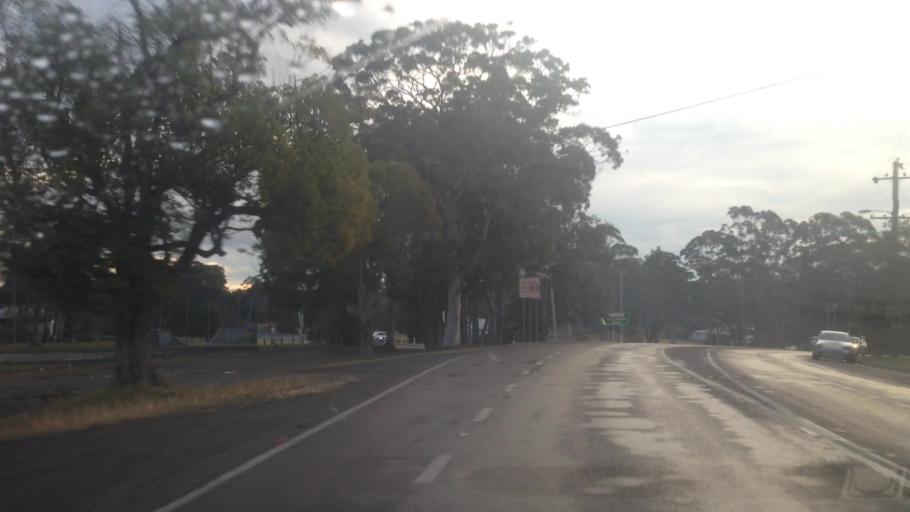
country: AU
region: New South Wales
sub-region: Wyong Shire
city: Charmhaven
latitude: -33.1760
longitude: 151.4822
